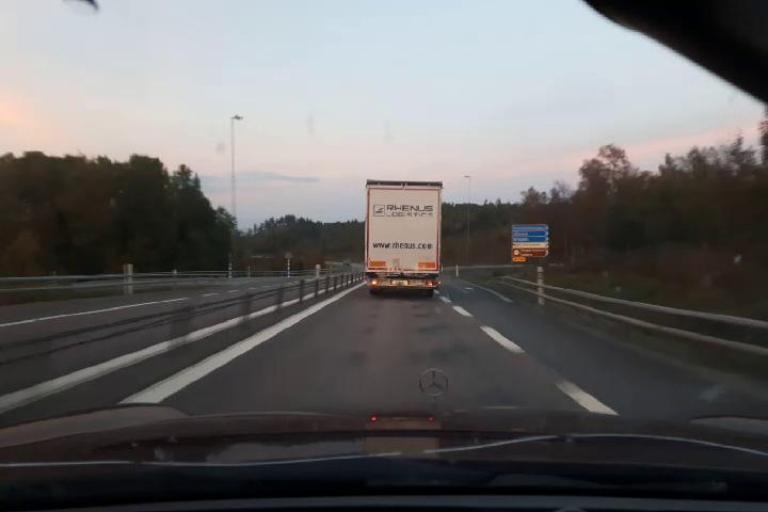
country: SE
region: Vaesternorrland
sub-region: Haernoesands Kommun
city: Haernoesand
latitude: 62.8122
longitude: 17.9634
